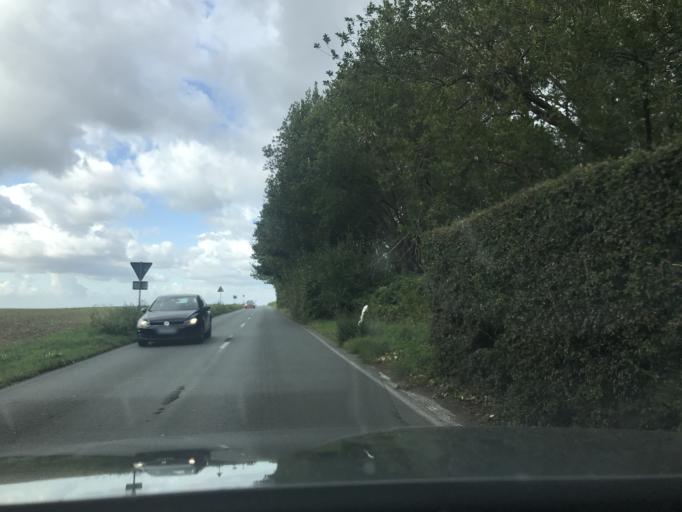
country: DE
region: North Rhine-Westphalia
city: Haan
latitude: 51.2113
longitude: 7.0018
